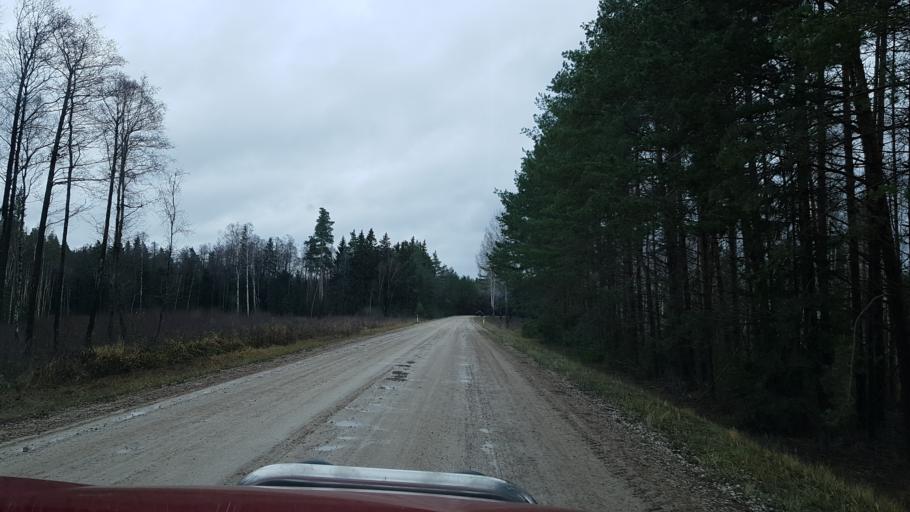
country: EE
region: Paernumaa
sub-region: Halinga vald
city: Parnu-Jaagupi
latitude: 58.5475
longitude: 24.4121
